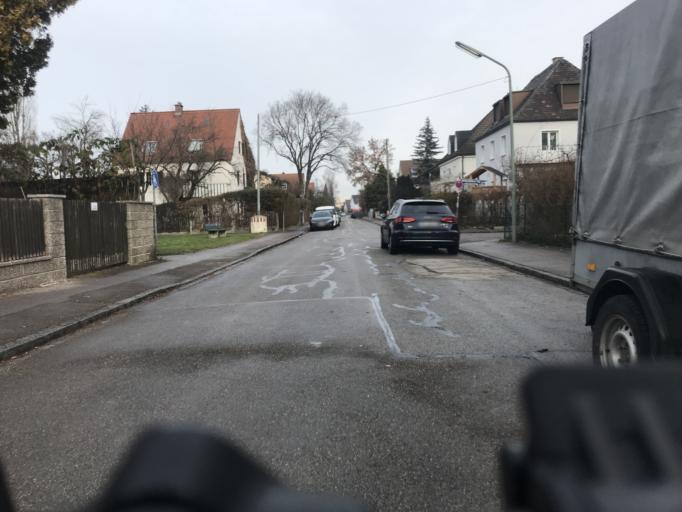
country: DE
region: Bavaria
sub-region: Upper Bavaria
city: Grafelfing
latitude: 48.1501
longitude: 11.4158
